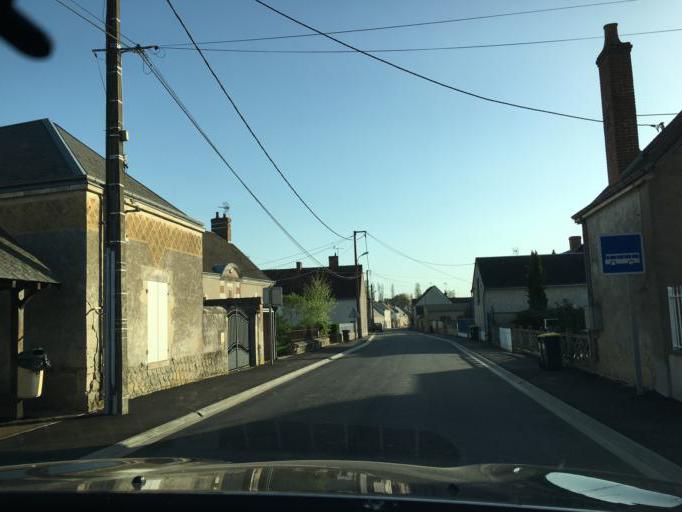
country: FR
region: Centre
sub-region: Departement du Loir-et-Cher
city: Ouzouer-le-Marche
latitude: 47.8980
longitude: 1.5744
